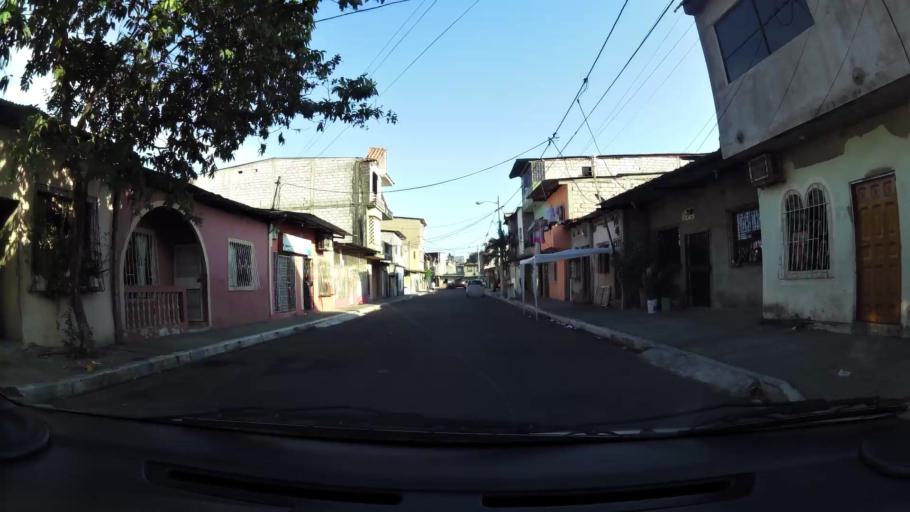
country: EC
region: Guayas
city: Guayaquil
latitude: -2.2285
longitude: -79.9102
